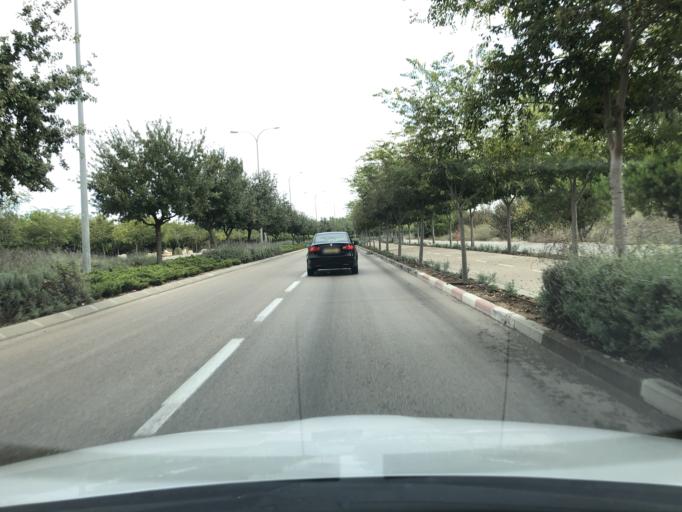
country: PS
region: West Bank
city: Al Midyah
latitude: 31.9213
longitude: 34.9953
